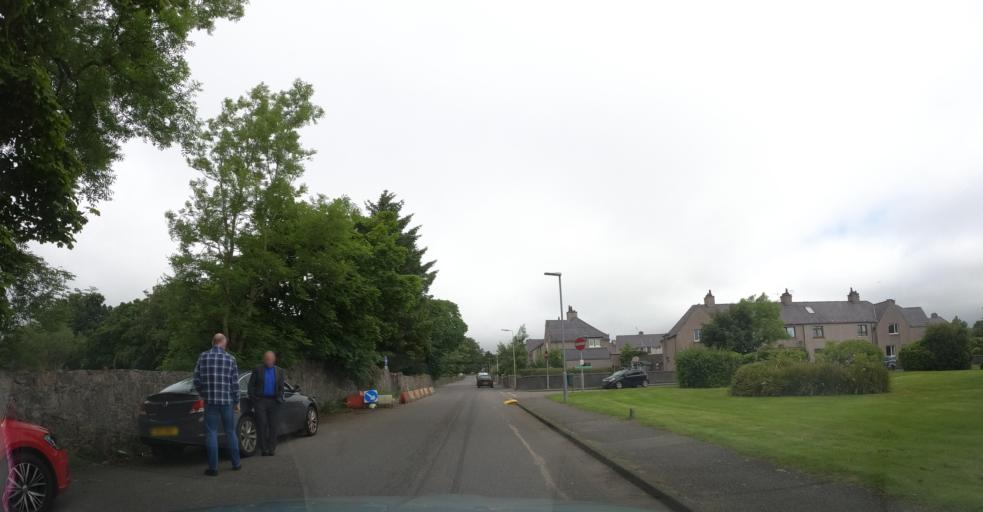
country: GB
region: Scotland
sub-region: Eilean Siar
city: Isle of Lewis
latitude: 58.2172
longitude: -6.3870
